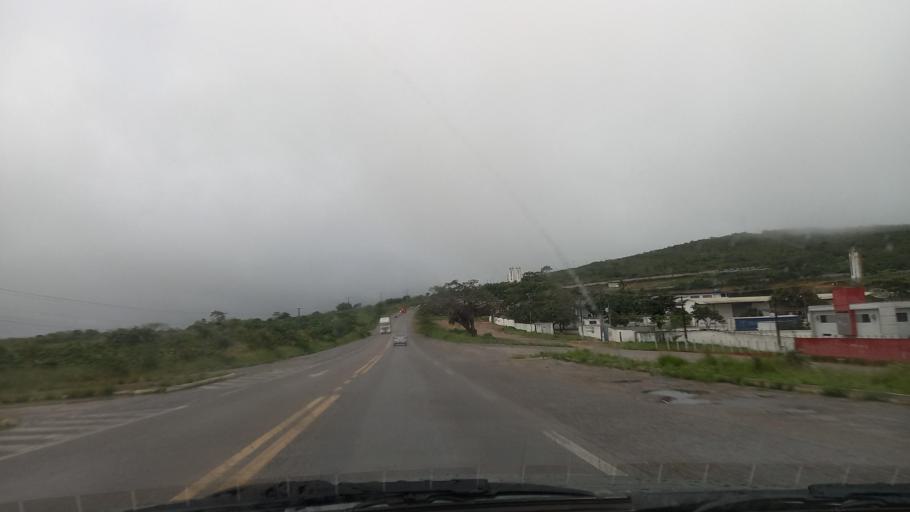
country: BR
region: Pernambuco
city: Garanhuns
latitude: -8.8746
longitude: -36.5252
